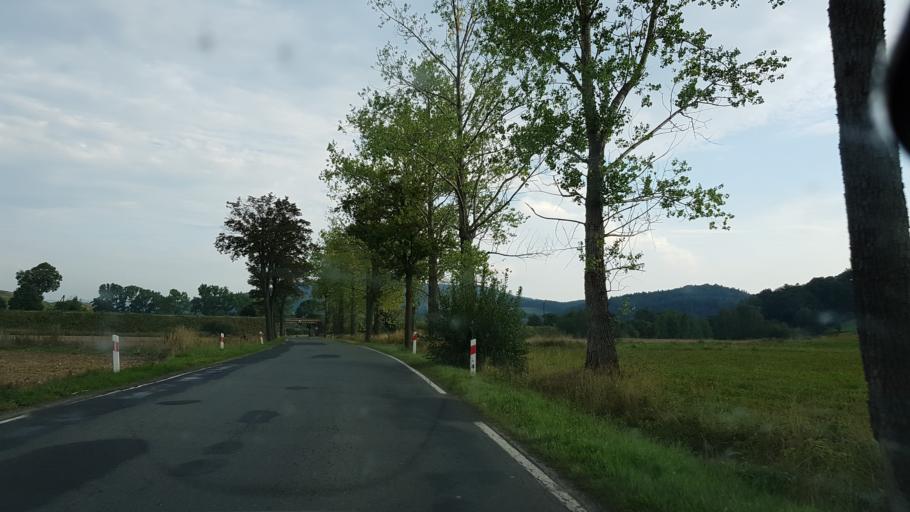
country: PL
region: Lower Silesian Voivodeship
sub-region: Powiat kamiennogorski
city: Marciszow
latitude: 50.8622
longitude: 16.0012
